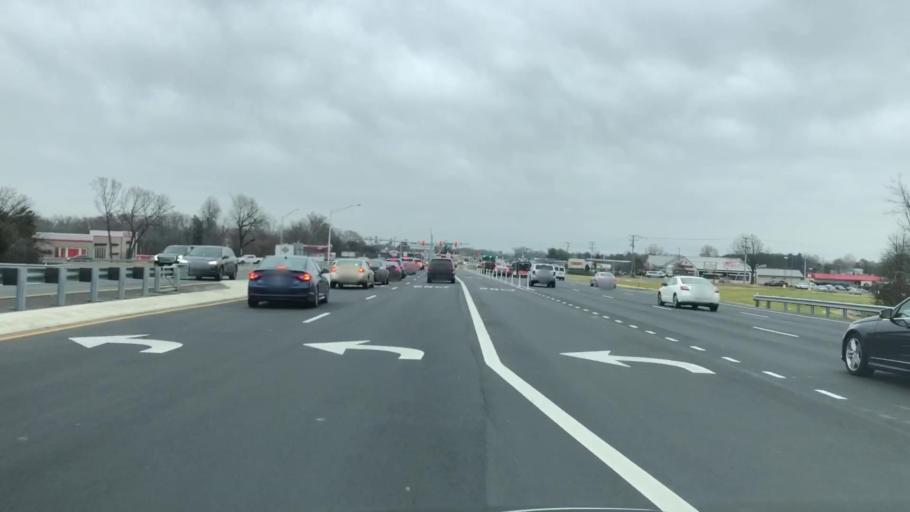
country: US
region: Virginia
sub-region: City of Fredericksburg
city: Fredericksburg
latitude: 38.2962
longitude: -77.5040
